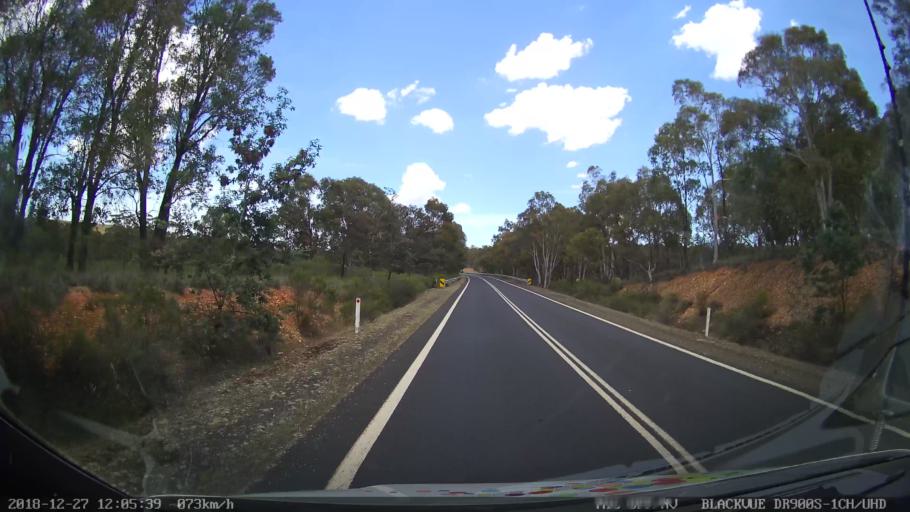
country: AU
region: New South Wales
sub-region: Blayney
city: Blayney
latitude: -33.8033
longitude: 149.3364
